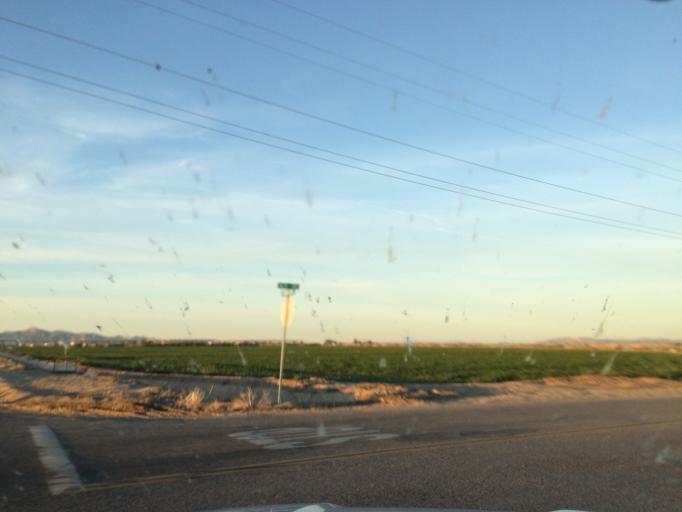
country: US
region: California
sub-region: Riverside County
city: Blythe
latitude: 33.5738
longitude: -114.6045
